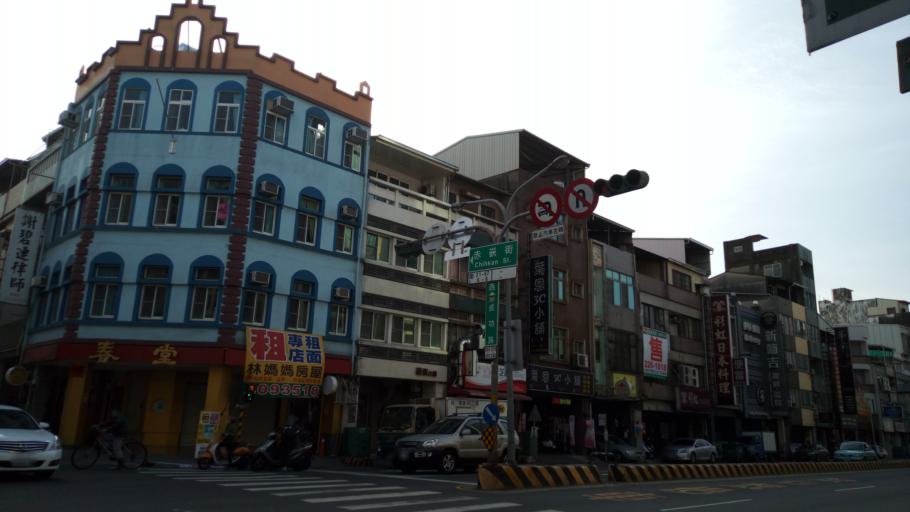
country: TW
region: Taiwan
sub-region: Tainan
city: Tainan
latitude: 22.9994
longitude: 120.2028
